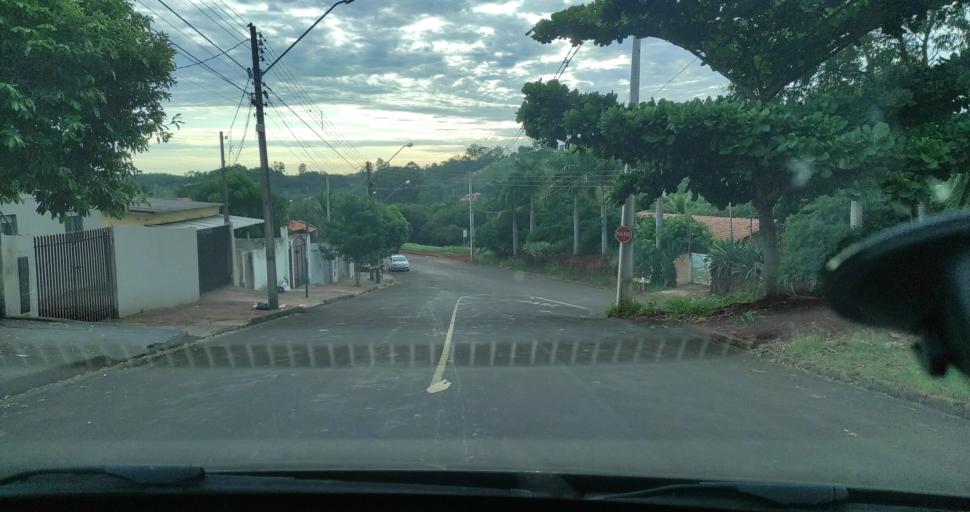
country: BR
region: Parana
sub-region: Ibipora
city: Ibipora
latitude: -23.2619
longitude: -51.0471
